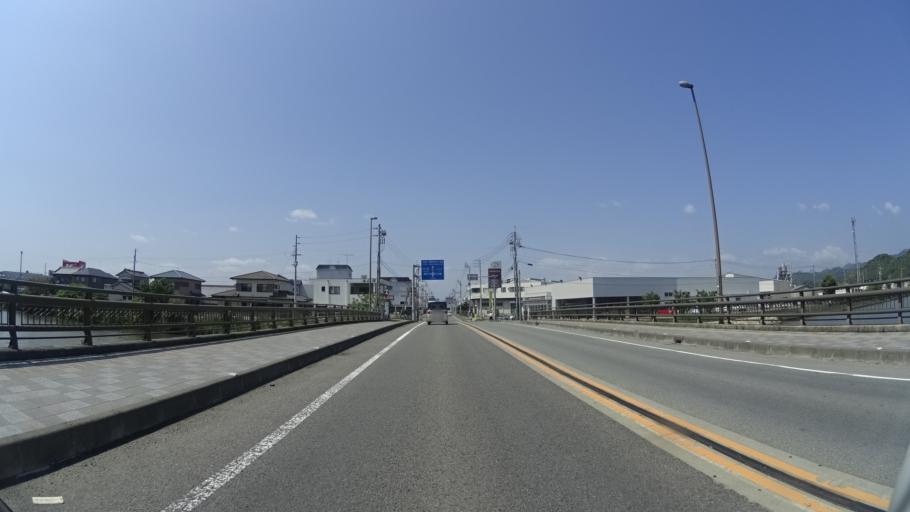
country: JP
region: Tokushima
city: Narutocho-mitsuishi
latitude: 34.1686
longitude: 134.6017
